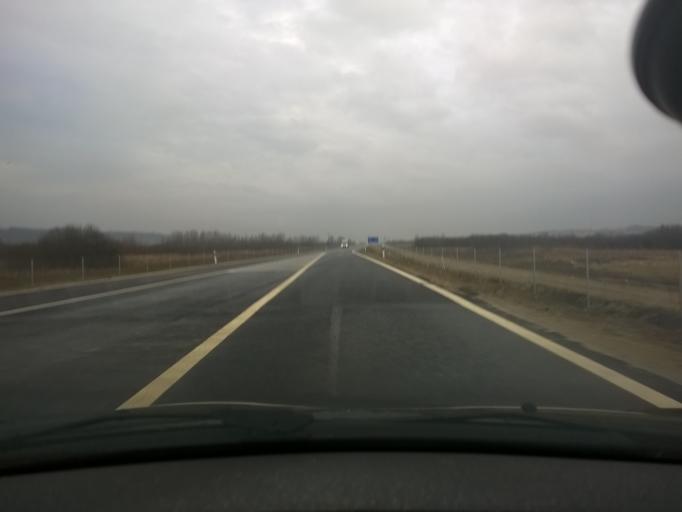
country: HR
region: Krapinsko-Zagorska
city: Bedekovcina
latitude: 46.0296
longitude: 15.9858
